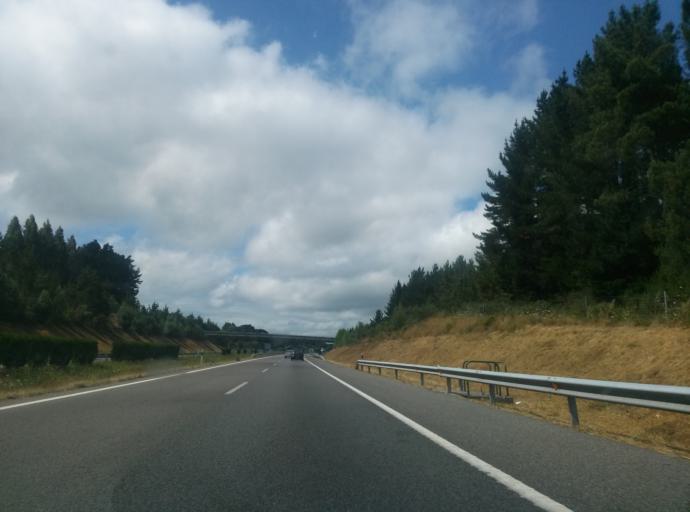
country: ES
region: Galicia
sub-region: Provincia de Lugo
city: Outeiro de Rei
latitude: 43.0732
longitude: -7.5751
